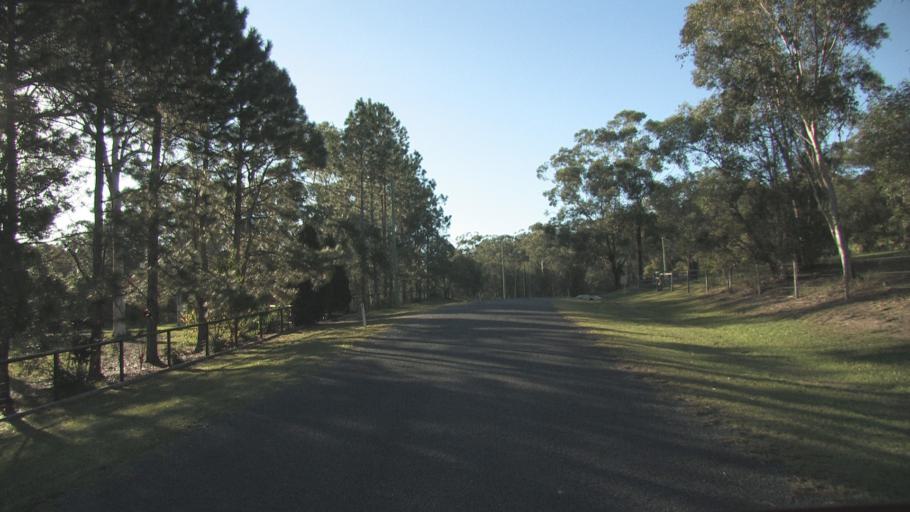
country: AU
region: Queensland
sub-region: Redland
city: Redland Bay
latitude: -27.6579
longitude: 153.2672
